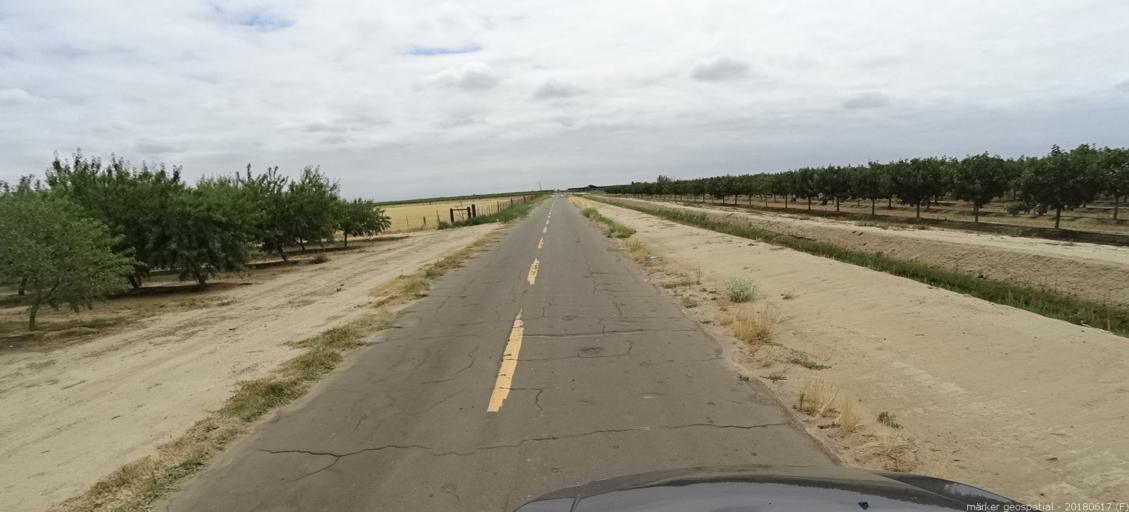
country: US
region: California
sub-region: Madera County
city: Fairmead
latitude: 37.0037
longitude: -120.1869
